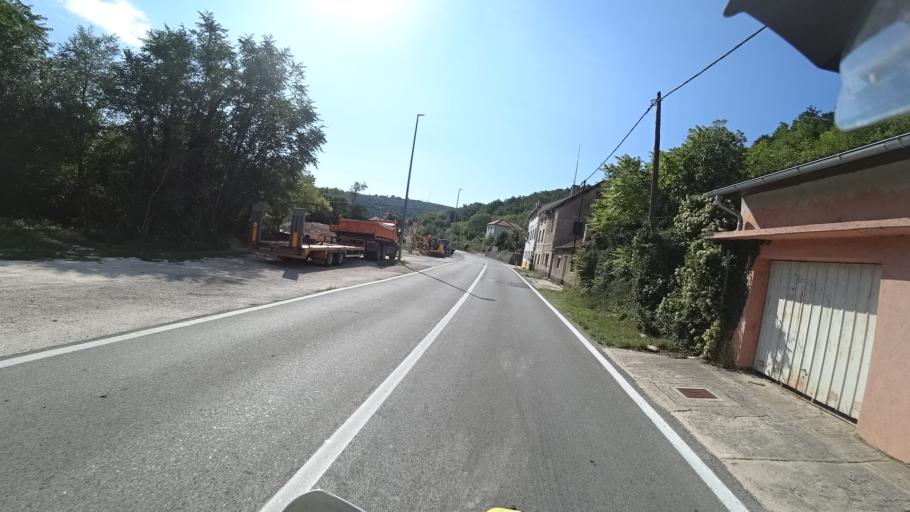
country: HR
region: Sibensko-Kniniska
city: Knin
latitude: 44.0312
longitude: 16.1899
